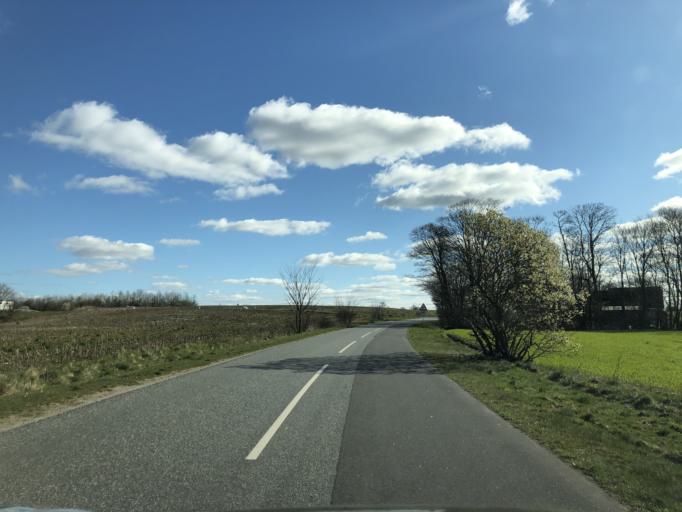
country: DK
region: North Denmark
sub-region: Vesthimmerland Kommune
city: Alestrup
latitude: 56.6143
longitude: 9.6139
